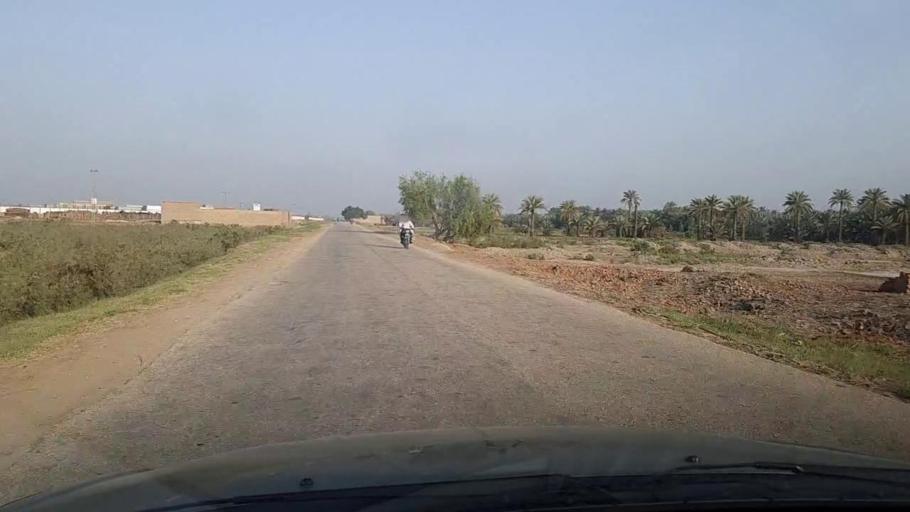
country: PK
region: Sindh
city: Khairpur
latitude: 27.5461
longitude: 68.7005
